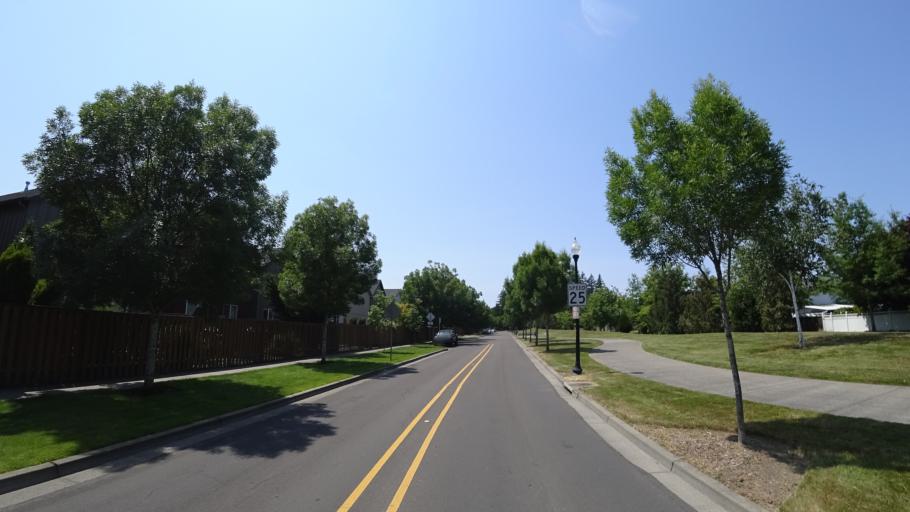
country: US
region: Oregon
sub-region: Washington County
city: Hillsboro
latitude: 45.4973
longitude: -122.9314
